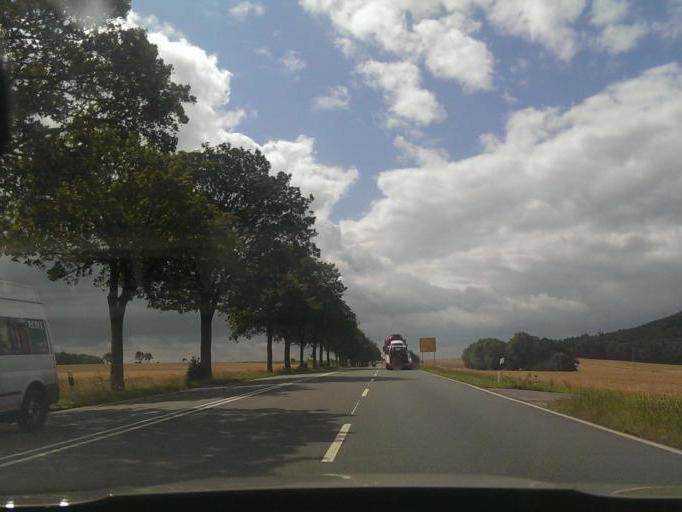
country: DE
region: Lower Saxony
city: Eschershausen
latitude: 51.9155
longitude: 9.6142
